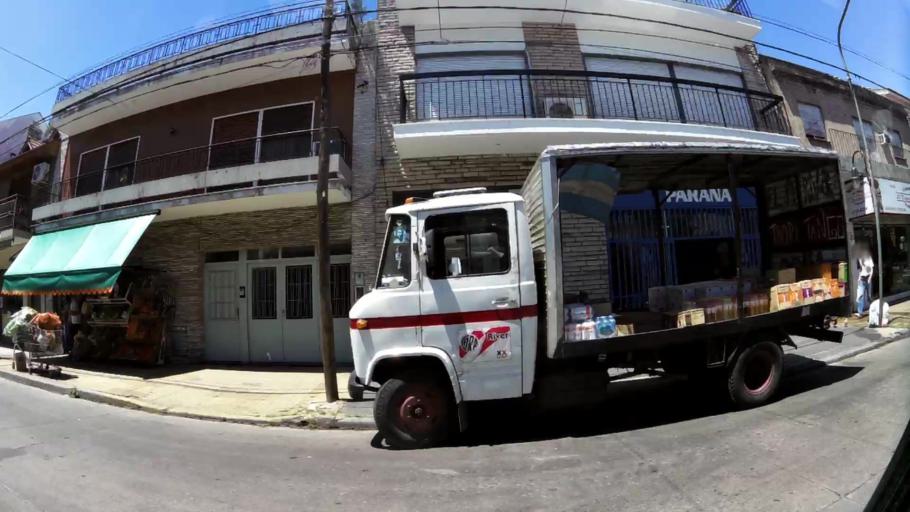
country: AR
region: Buenos Aires
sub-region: Partido de Vicente Lopez
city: Olivos
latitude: -34.5058
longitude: -58.5153
